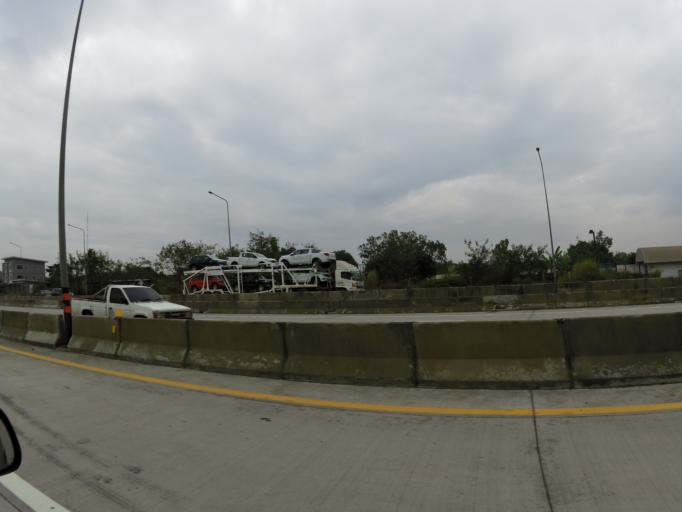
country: TH
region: Chon Buri
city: Ban Talat Bueng
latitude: 13.1152
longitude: 100.9708
